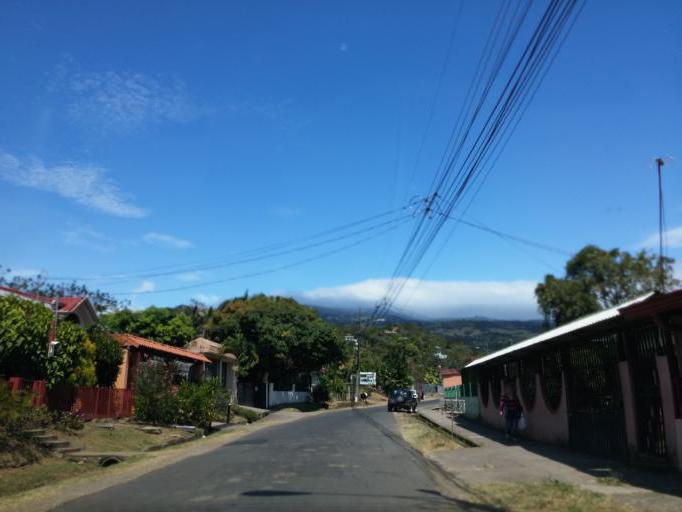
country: CR
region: Heredia
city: Santo Domingo
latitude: 10.0422
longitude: -84.1440
